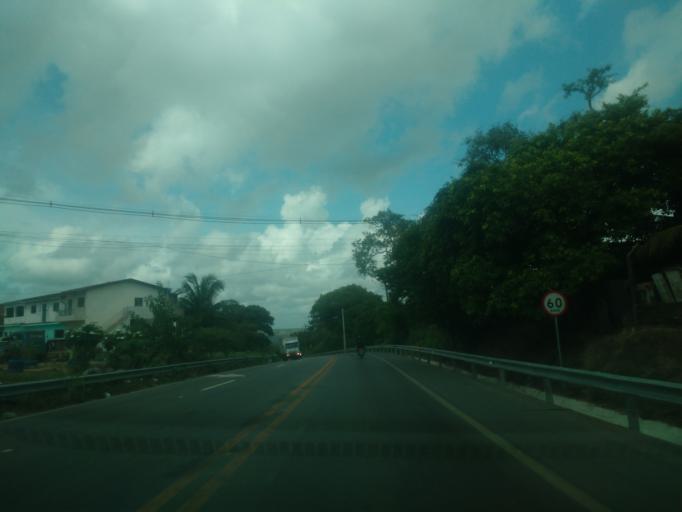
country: BR
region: Alagoas
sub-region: Satuba
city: Satuba
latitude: -9.5664
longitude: -35.7920
